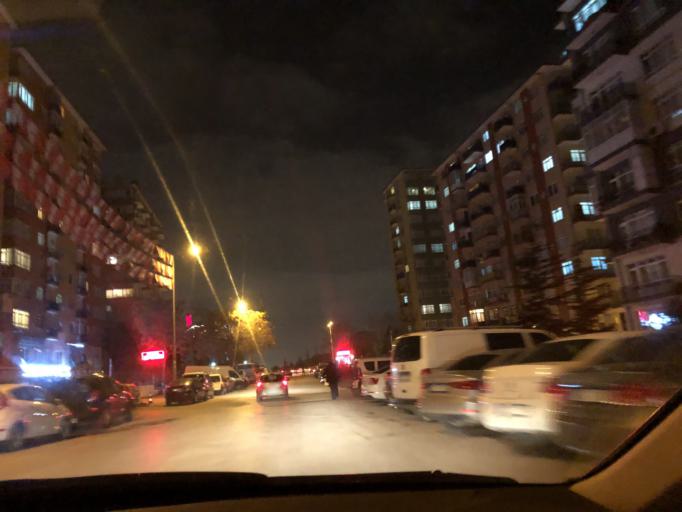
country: TR
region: Ankara
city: Batikent
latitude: 39.9648
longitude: 32.7961
